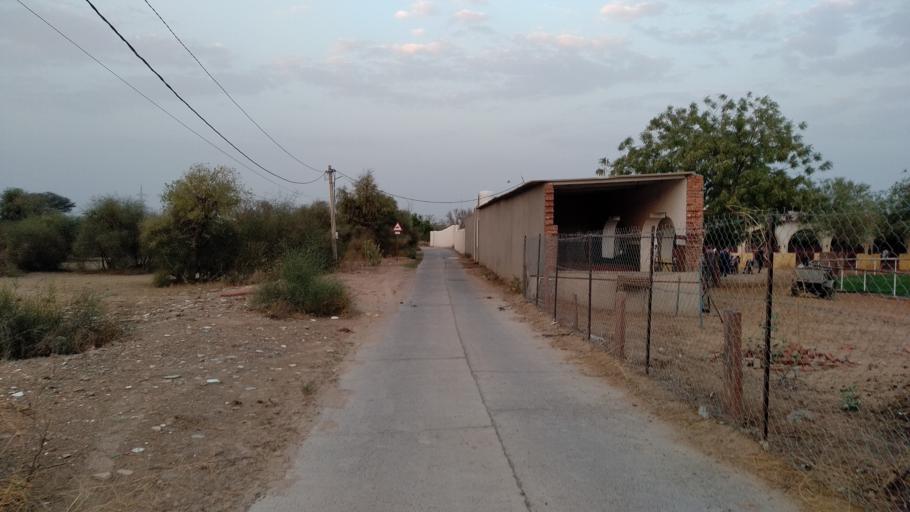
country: IN
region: Rajasthan
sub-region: Sikar
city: Fatehpur
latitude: 28.0412
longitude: 75.1503
